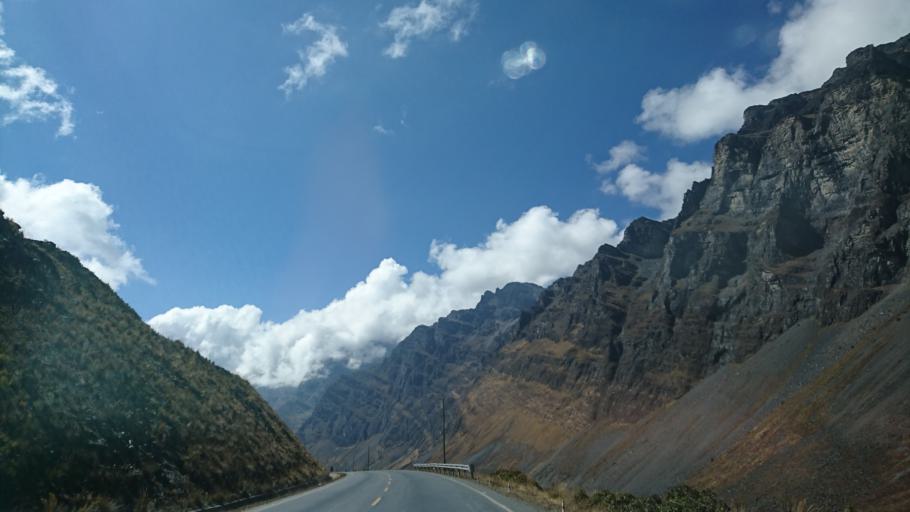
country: BO
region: La Paz
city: La Paz
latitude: -16.3270
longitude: -68.0003
